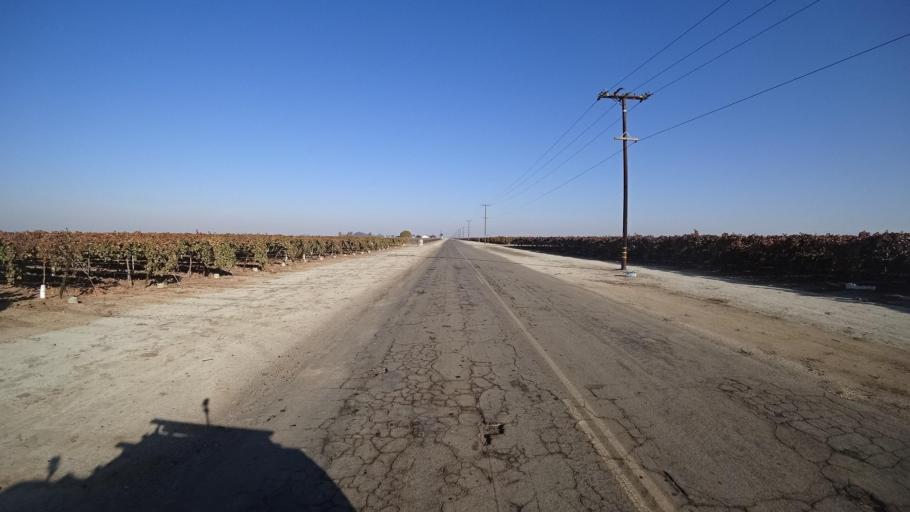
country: US
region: California
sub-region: Kern County
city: McFarland
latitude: 35.7244
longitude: -119.1695
